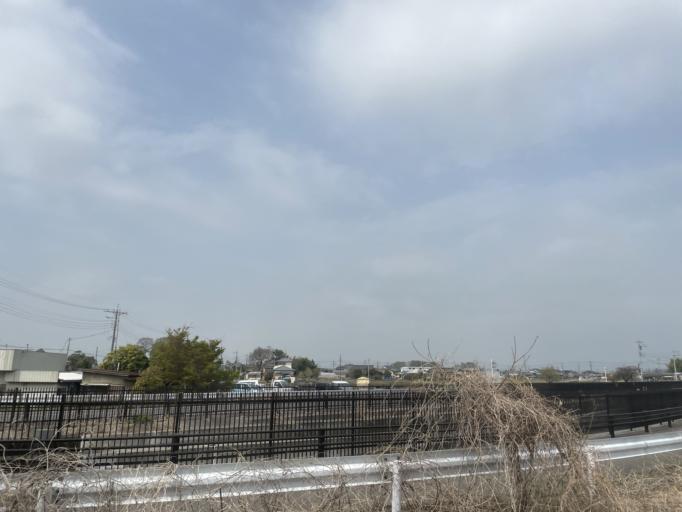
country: JP
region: Saitama
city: Gyoda
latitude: 36.1581
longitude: 139.4804
